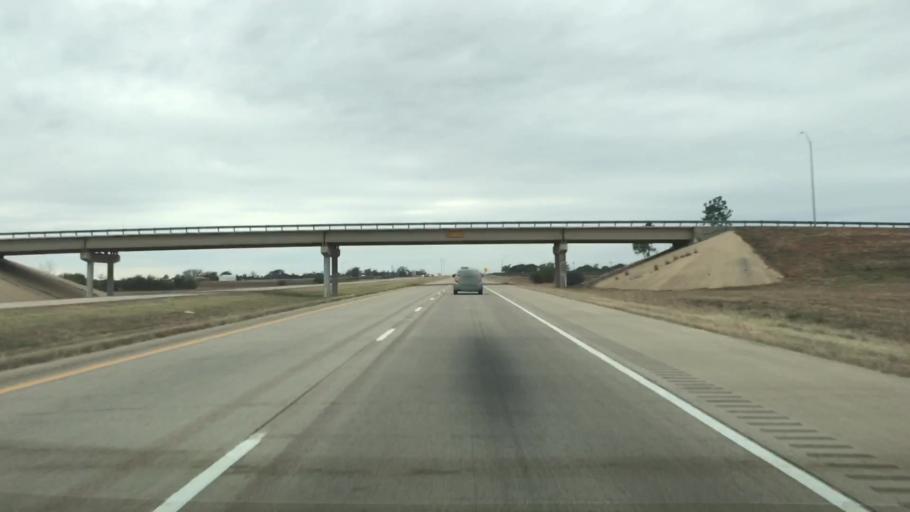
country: US
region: Texas
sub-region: Wheeler County
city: Shamrock
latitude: 35.2270
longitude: -100.1649
